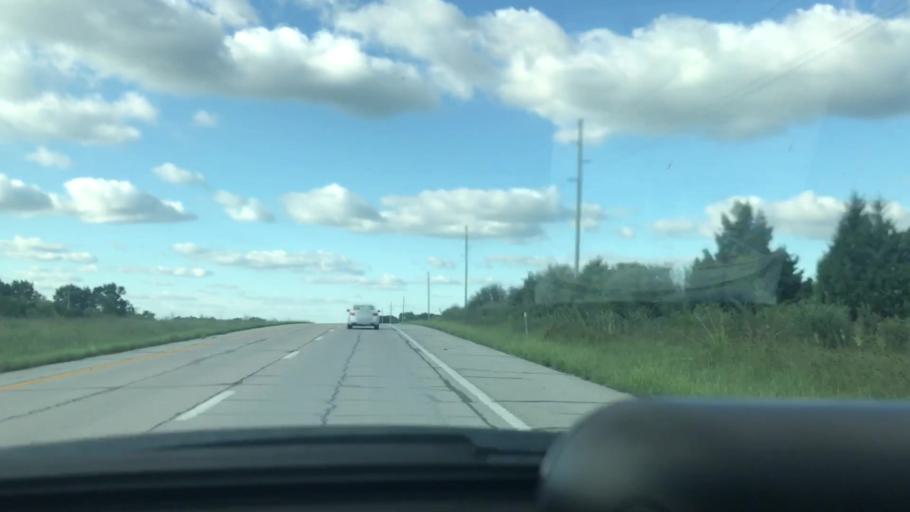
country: US
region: Missouri
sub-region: Pettis County
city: Sedalia
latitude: 38.6216
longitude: -93.2674
